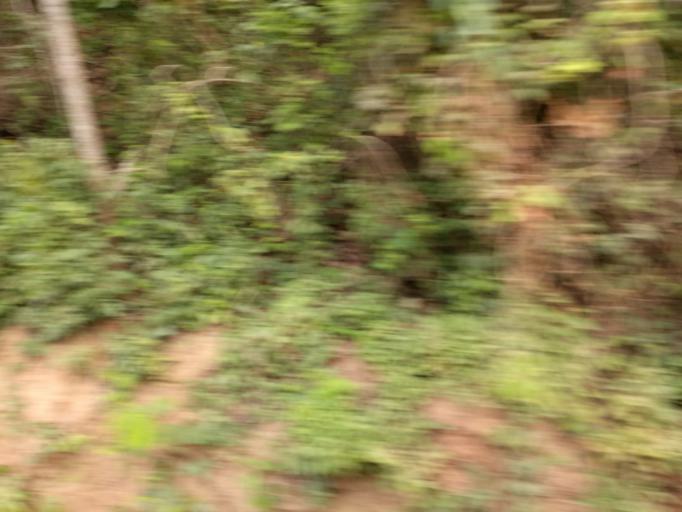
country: BO
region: Santa Cruz
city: Santiago del Torno
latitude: -17.9303
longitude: -63.4124
